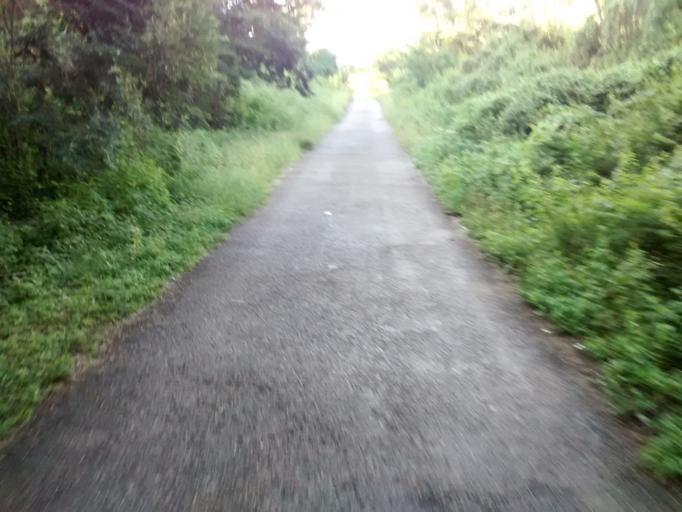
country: MX
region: Yucatan
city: Valladolid
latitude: 20.7151
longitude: -88.2212
